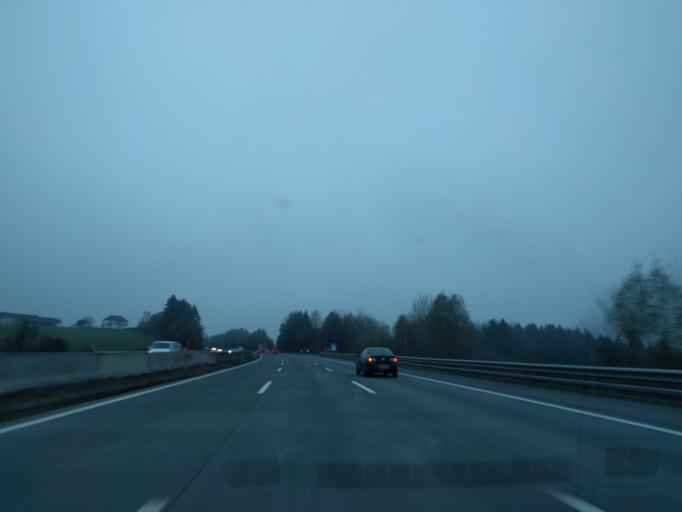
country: AT
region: Lower Austria
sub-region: Politischer Bezirk Amstetten
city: Sankt Georgen am Ybbsfelde
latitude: 48.1447
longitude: 14.9152
